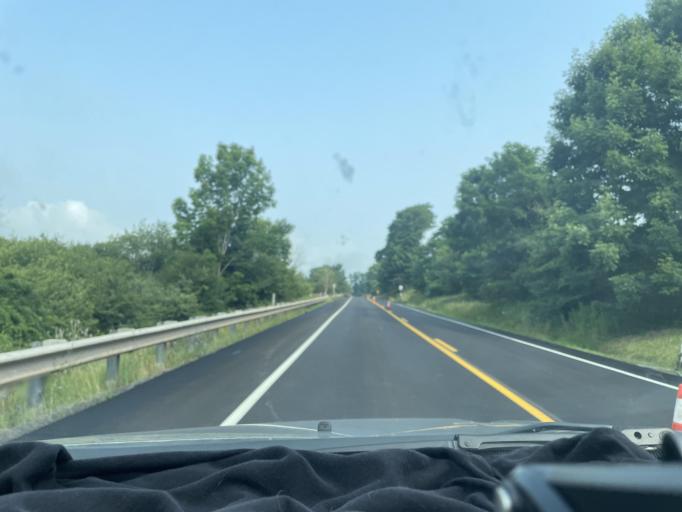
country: US
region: Maryland
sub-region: Garrett County
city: Mountain Lake Park
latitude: 39.2902
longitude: -79.3522
